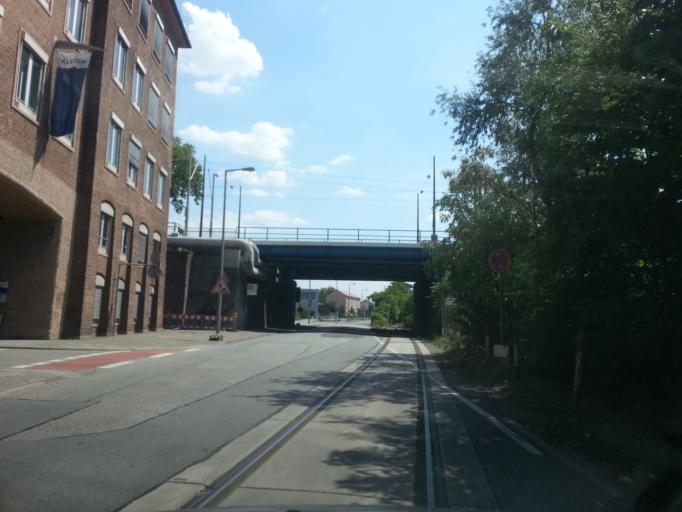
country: DE
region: Baden-Wuerttemberg
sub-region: Karlsruhe Region
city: Mannheim
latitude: 49.5055
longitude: 8.5012
